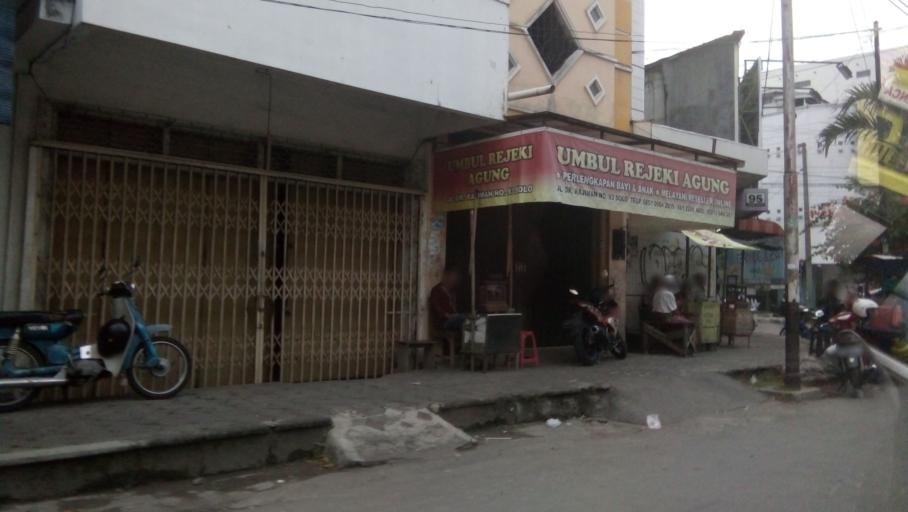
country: ID
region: Central Java
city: Surakarta
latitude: -7.5744
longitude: 110.8234
